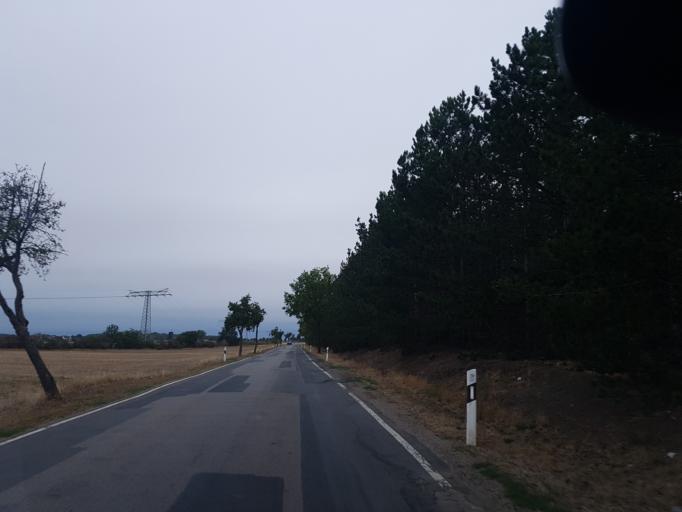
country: DE
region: Saxony
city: Arzberg
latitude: 51.5324
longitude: 13.1216
